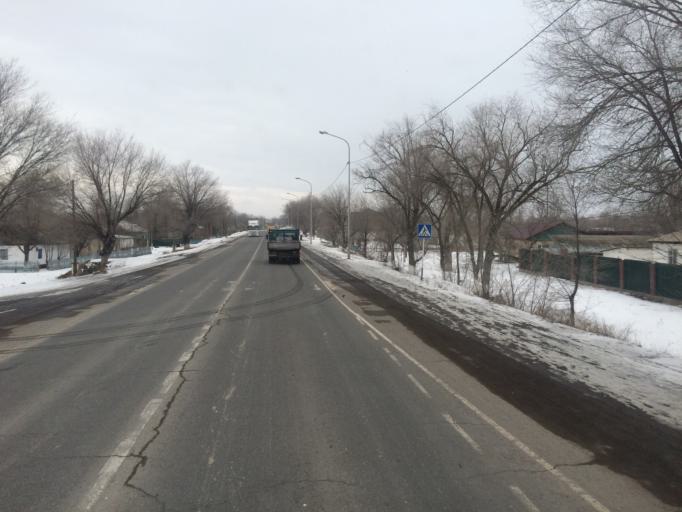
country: KG
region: Chuy
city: Bystrovka
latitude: 43.3334
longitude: 75.8491
